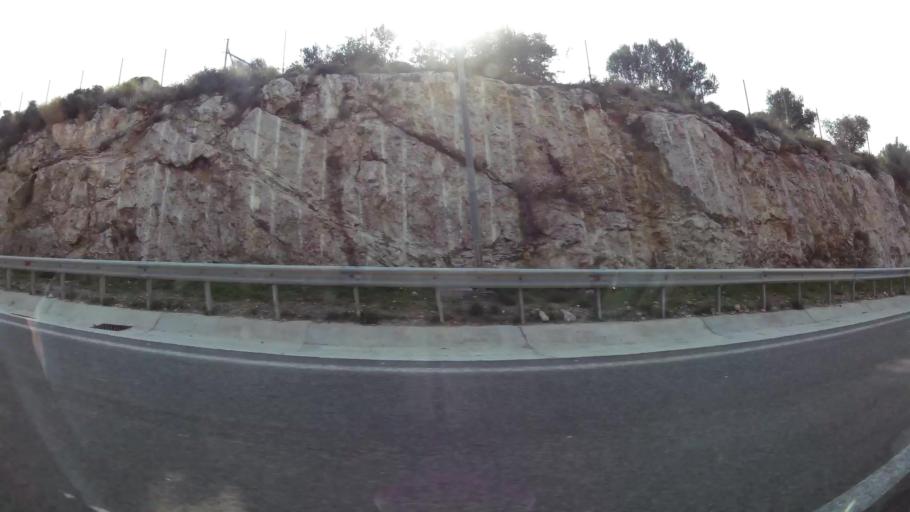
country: GR
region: Attica
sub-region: Nomarchia Athinas
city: Petroupolis
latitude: 38.0567
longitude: 23.6590
